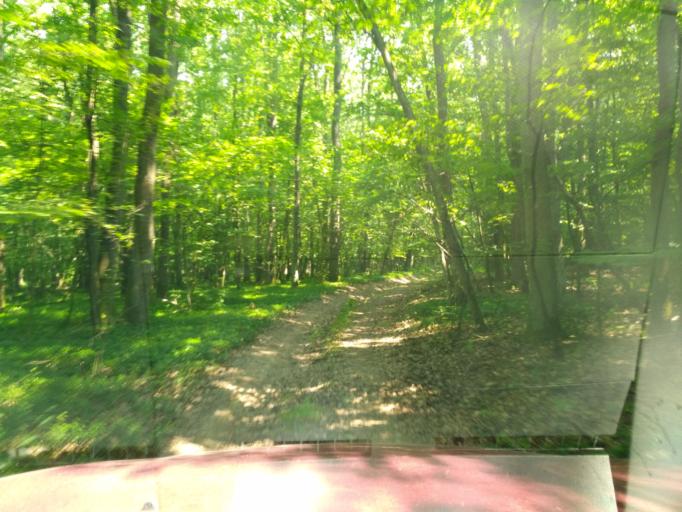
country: SK
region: Kosicky
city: Moldava nad Bodvou
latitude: 48.6190
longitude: 21.0435
